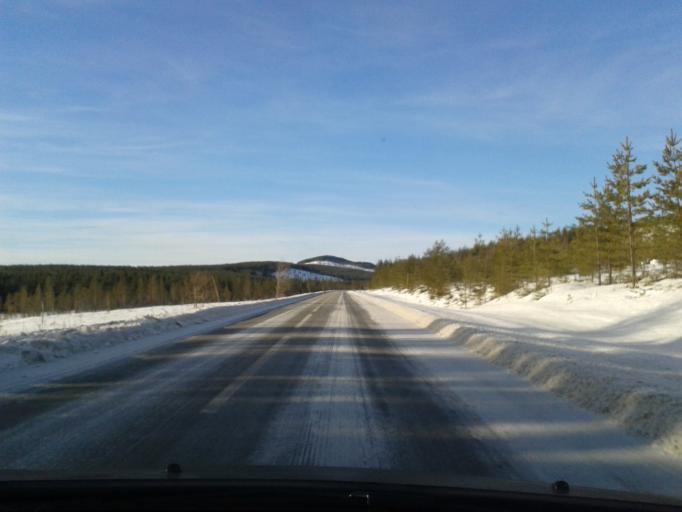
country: SE
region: Vaesternorrland
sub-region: OErnskoeldsviks Kommun
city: Bredbyn
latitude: 63.7523
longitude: 17.7108
